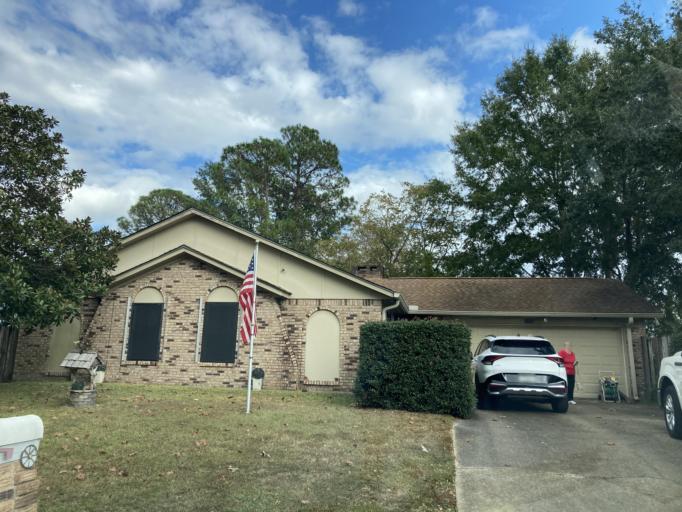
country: US
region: Mississippi
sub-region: Jackson County
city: Gulf Hills
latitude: 30.4362
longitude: -88.8200
